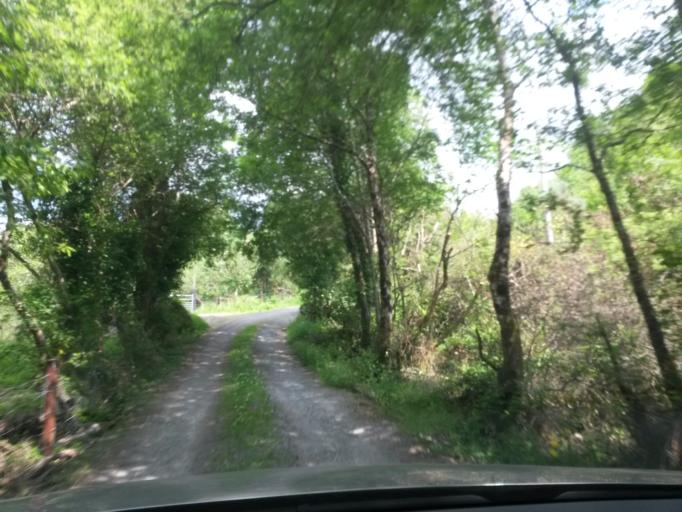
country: IE
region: Munster
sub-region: Ciarrai
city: Kenmare
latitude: 51.8154
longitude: -9.5237
